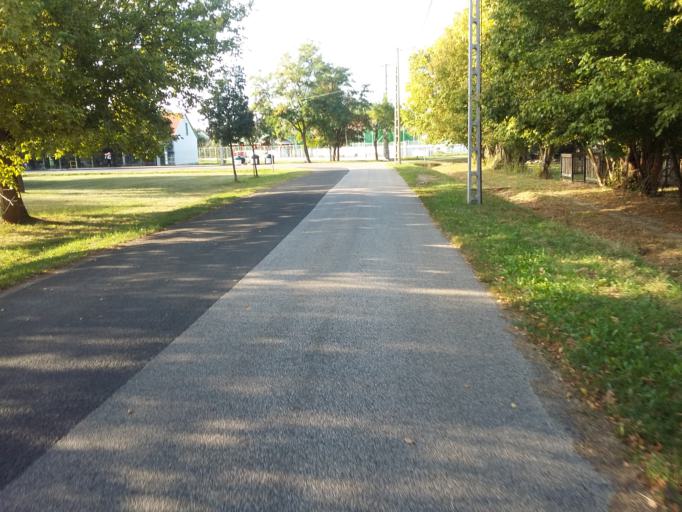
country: HU
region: Csongrad
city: Szeged
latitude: 46.2052
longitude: 20.1104
